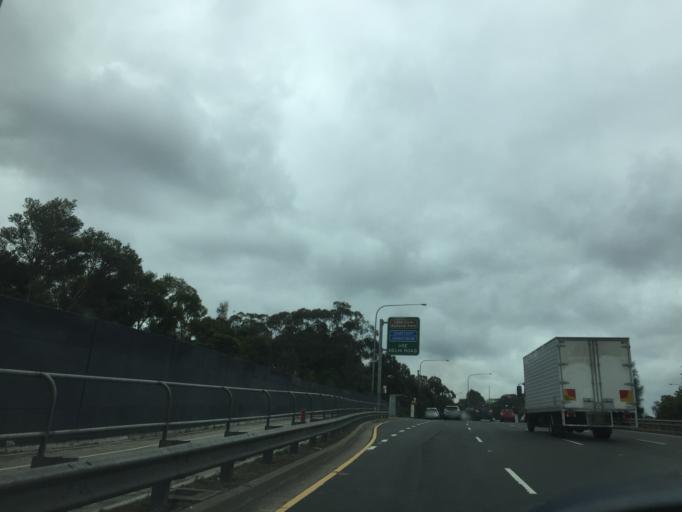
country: AU
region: New South Wales
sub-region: Ryde
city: East Ryde
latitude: -33.7981
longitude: 151.1384
